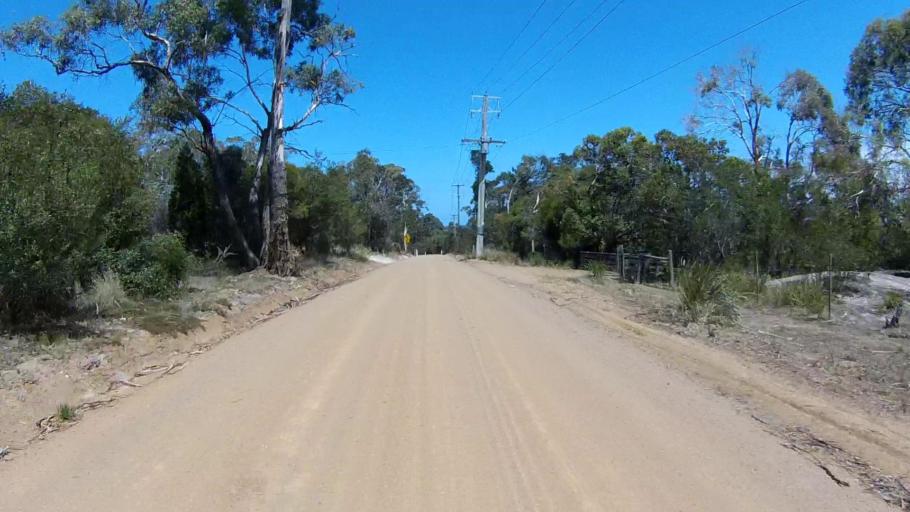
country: AU
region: Tasmania
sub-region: Clarence
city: Lauderdale
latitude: -42.9395
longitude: 147.4605
